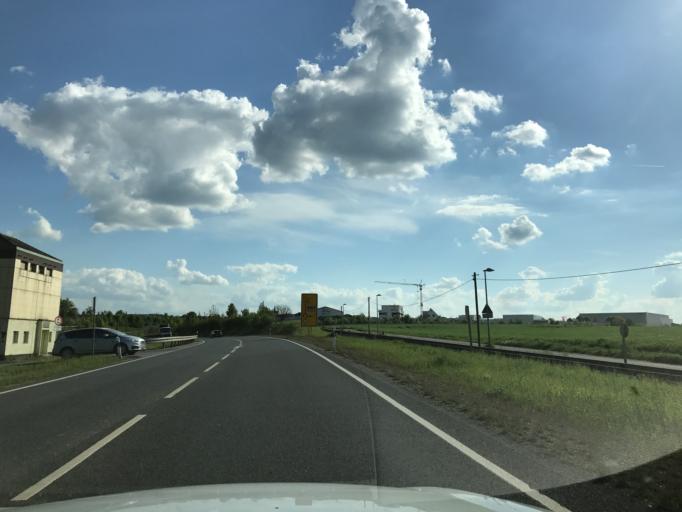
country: DE
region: Bavaria
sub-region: Upper Franconia
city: Igensdorf
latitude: 49.5824
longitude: 11.2068
